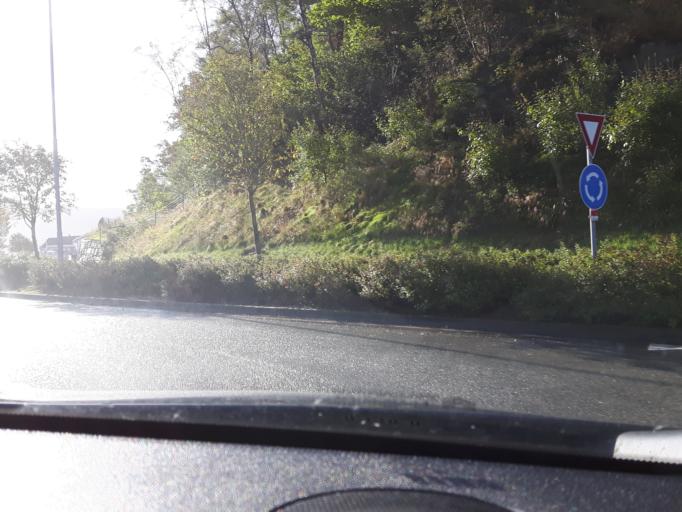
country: NO
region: Rogaland
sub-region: Gjesdal
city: Algard
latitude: 58.7690
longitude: 5.8569
